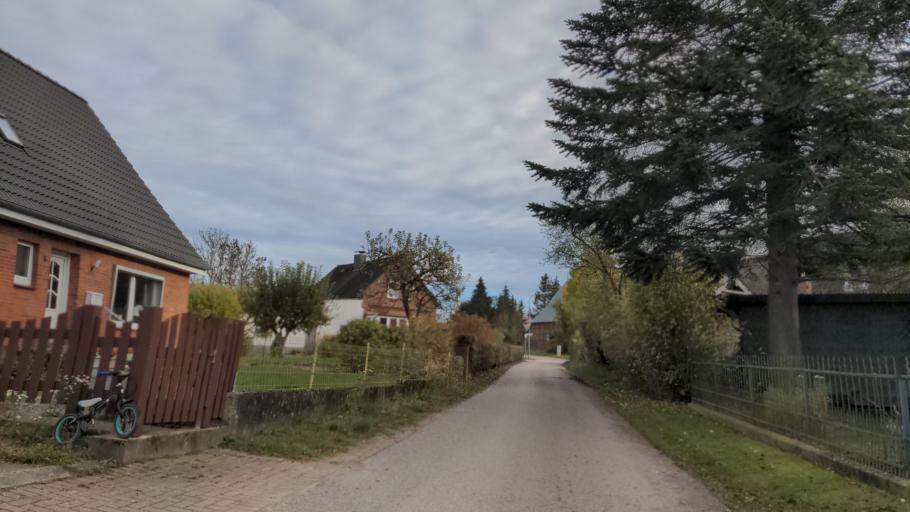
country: DE
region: Schleswig-Holstein
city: Bosdorf
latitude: 54.1112
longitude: 10.4987
